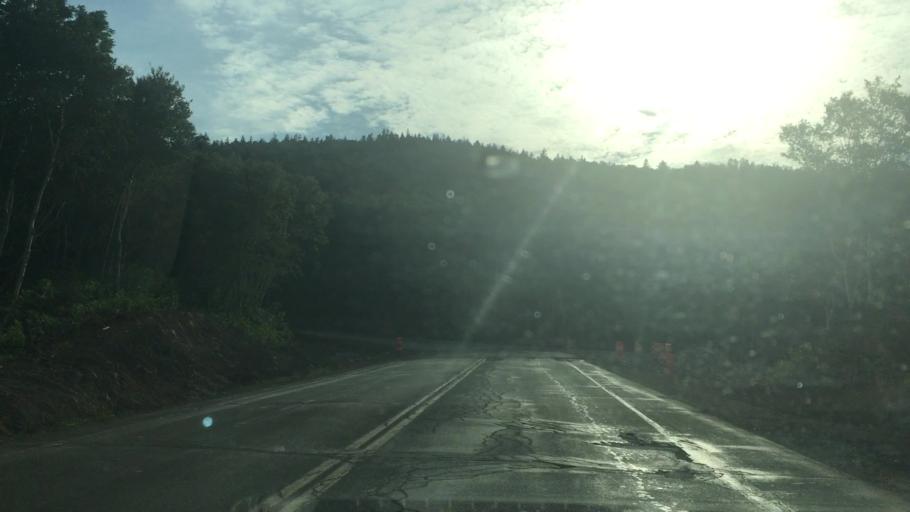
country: CA
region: Nova Scotia
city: Sydney Mines
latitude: 46.8201
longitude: -60.8358
